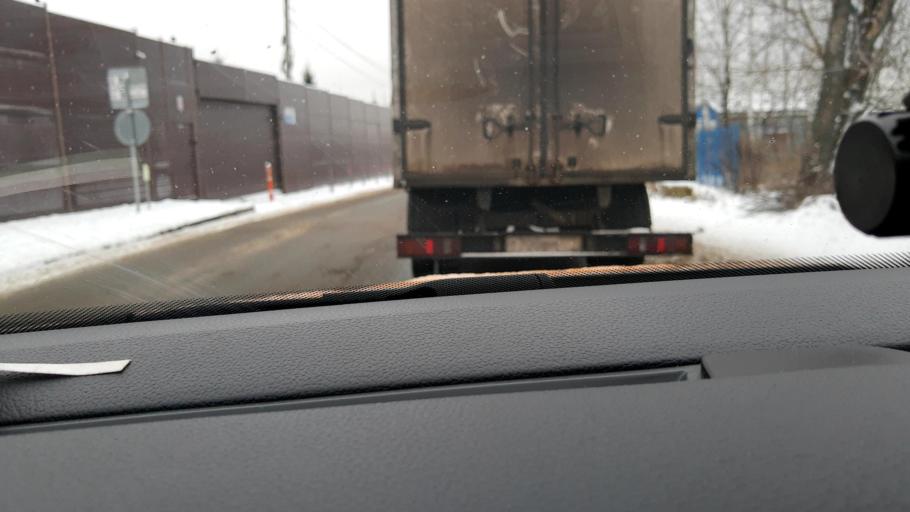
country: RU
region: Moskovskaya
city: Povedniki
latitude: 55.9305
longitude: 37.6323
